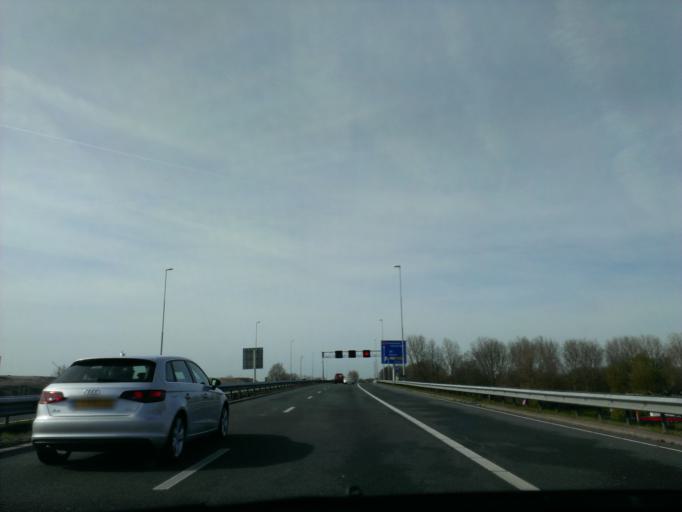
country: NL
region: North Holland
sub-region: Gemeente Amsterdam
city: Driemond
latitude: 52.3190
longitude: 4.9992
